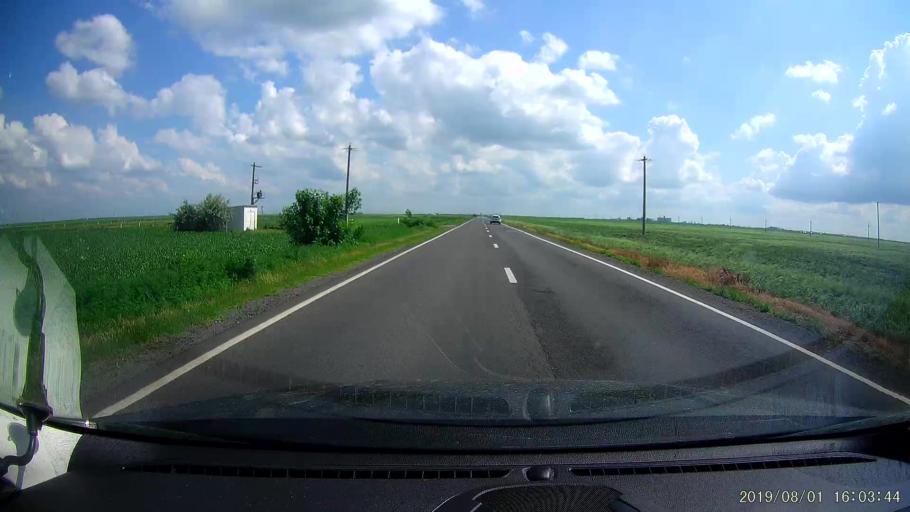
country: RO
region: Calarasi
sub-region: Comuna Dragalina
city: Drajna Noua
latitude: 44.4647
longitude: 27.3831
